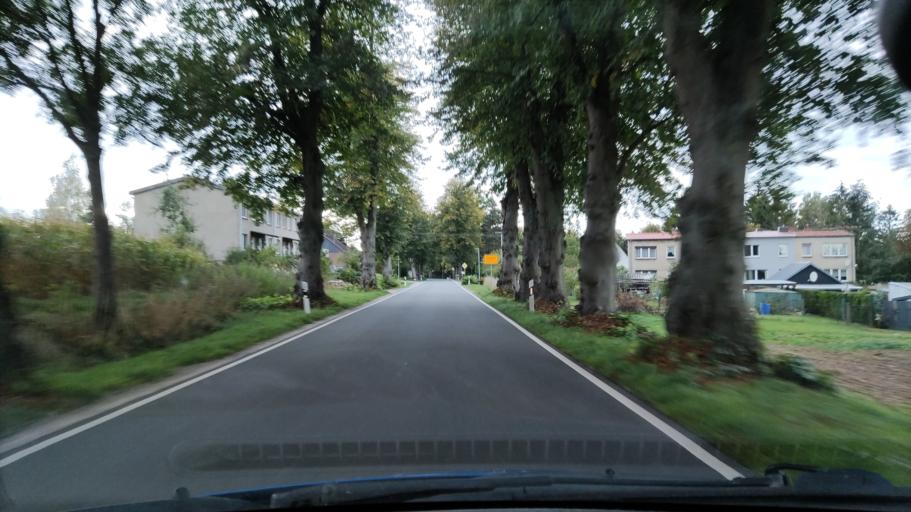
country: DE
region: Mecklenburg-Vorpommern
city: Zarrentin
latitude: 53.4624
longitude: 10.9711
